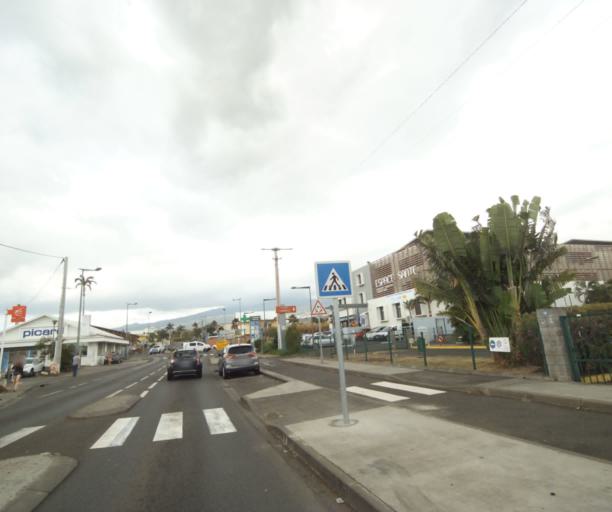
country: RE
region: Reunion
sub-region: Reunion
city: Saint-Paul
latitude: -20.9862
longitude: 55.2963
